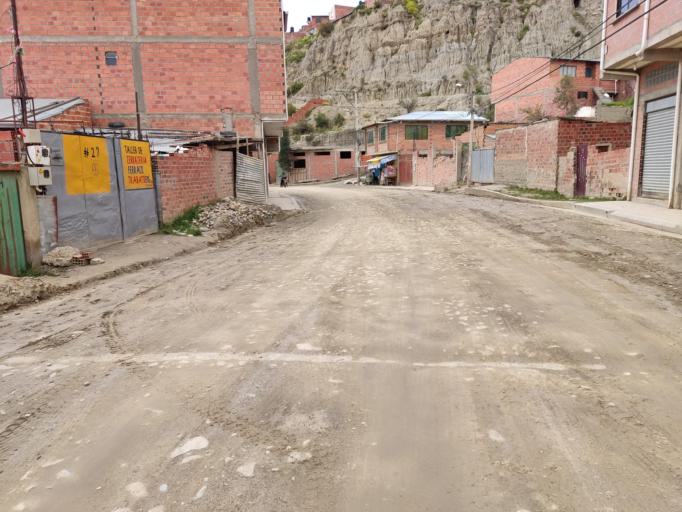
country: BO
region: La Paz
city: La Paz
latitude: -16.5364
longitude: -68.1340
